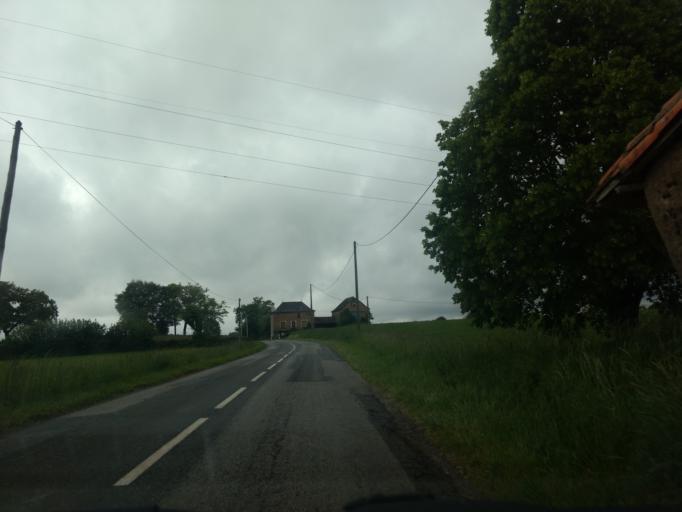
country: FR
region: Midi-Pyrenees
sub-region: Departement de l'Aveyron
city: Montbazens
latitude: 44.5078
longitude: 2.1929
